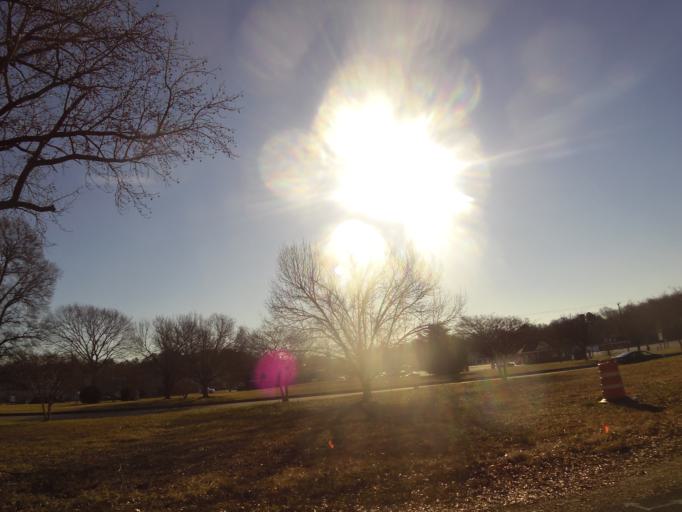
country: US
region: Virginia
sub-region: Prince George County
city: Fort Lee
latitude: 37.2705
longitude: -77.3192
